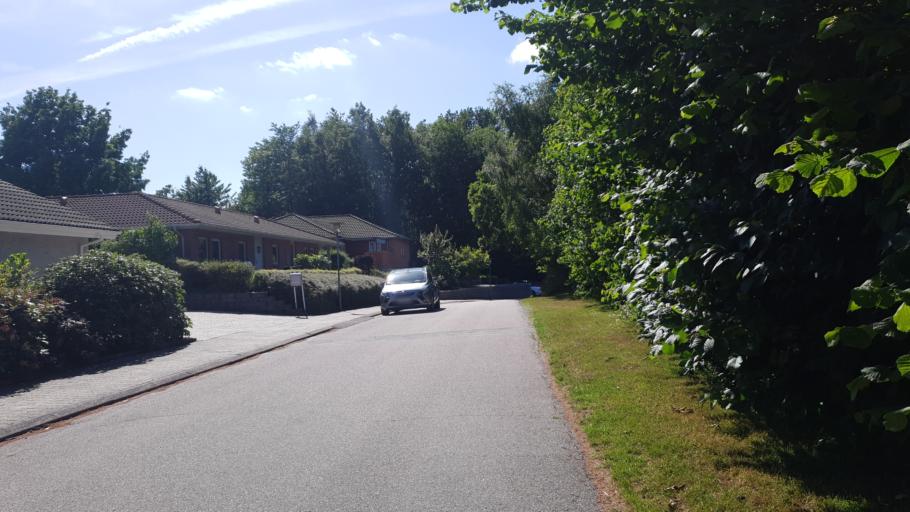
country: DK
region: South Denmark
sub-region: Fredericia Kommune
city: Snoghoj
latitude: 55.5345
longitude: 9.7325
